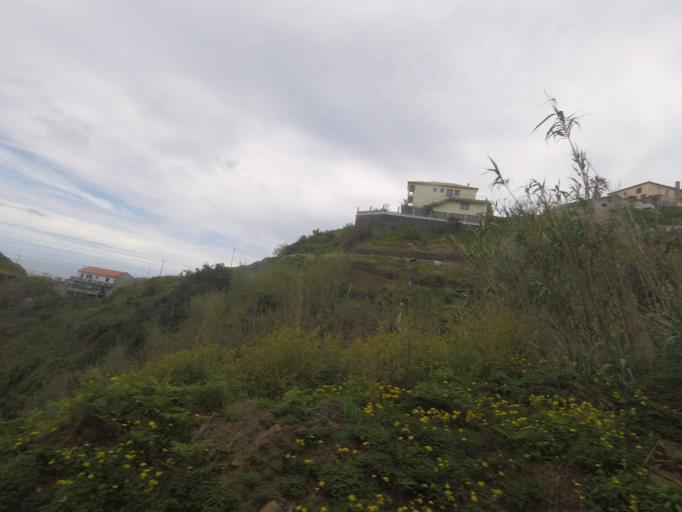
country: PT
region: Madeira
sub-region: Santana
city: Santana
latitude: 32.7649
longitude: -16.8193
